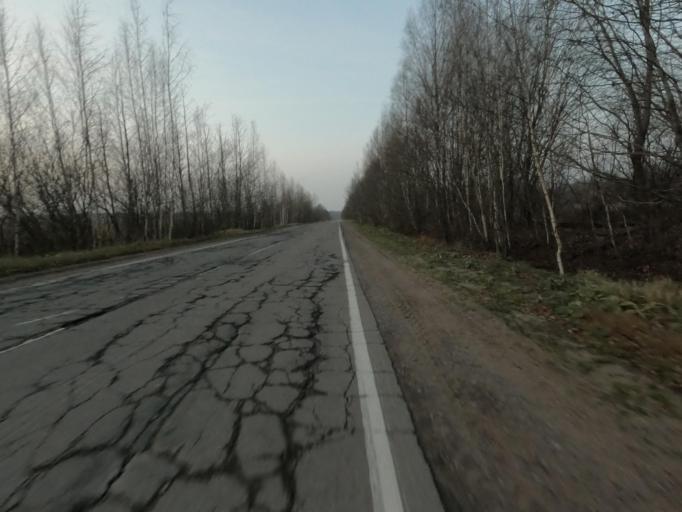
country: RU
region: Leningrad
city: Kirovsk
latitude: 59.8601
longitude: 30.9811
